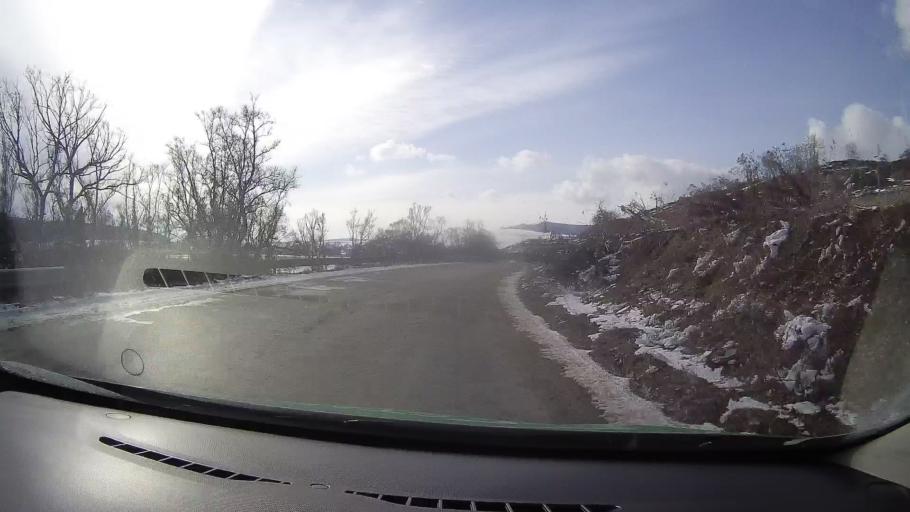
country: RO
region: Sibiu
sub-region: Comuna Iacobeni
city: Iacobeni
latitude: 46.0418
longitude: 24.7401
